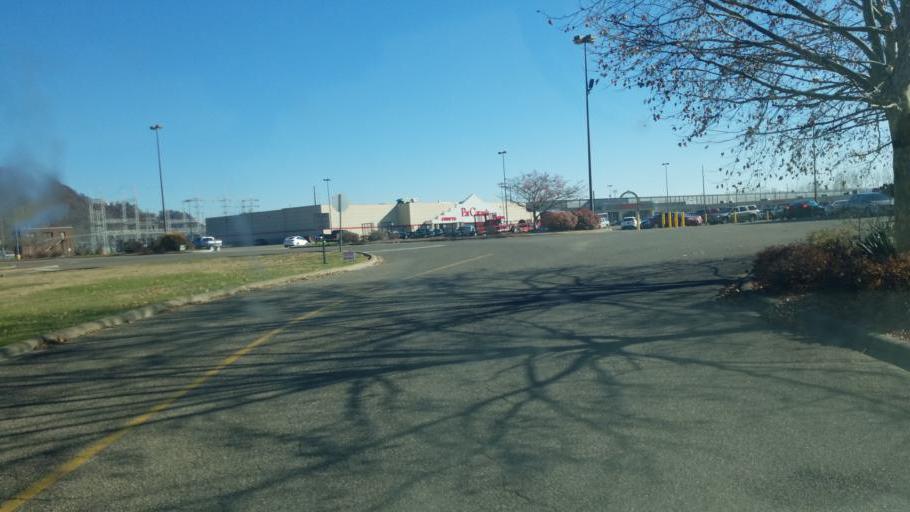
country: US
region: Ohio
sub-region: Scioto County
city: New Boston
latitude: 38.7522
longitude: -82.9340
